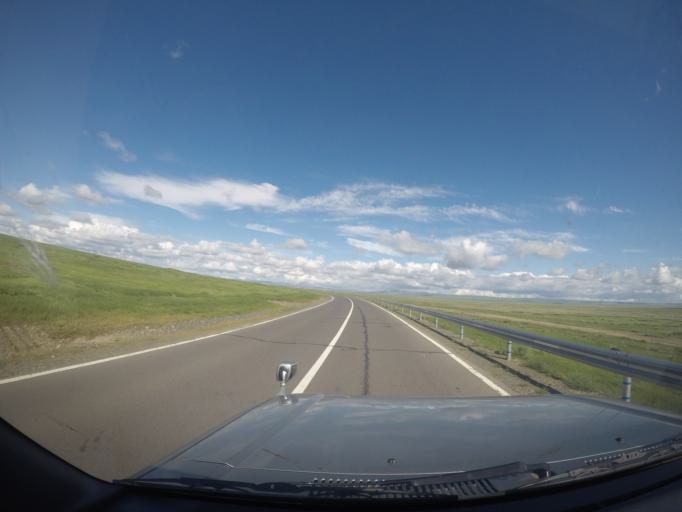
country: MN
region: Hentiy
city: Moron
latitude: 47.4174
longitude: 109.8672
